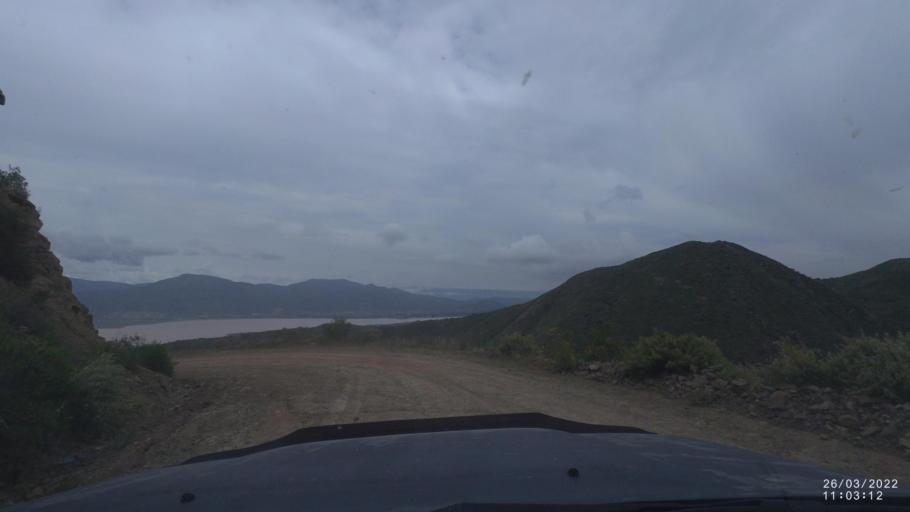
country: BO
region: Cochabamba
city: Tarata
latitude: -17.5257
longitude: -66.0253
